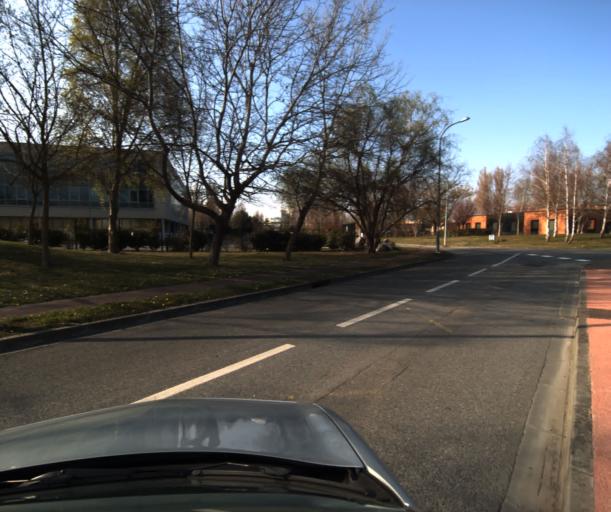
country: FR
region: Midi-Pyrenees
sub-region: Departement de la Haute-Garonne
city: Ramonville-Saint-Agne
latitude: 43.5512
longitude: 1.4878
